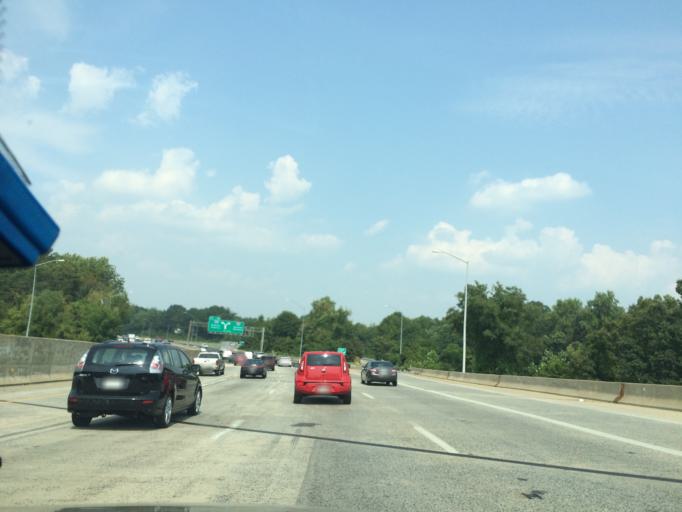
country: US
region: Maryland
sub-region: Montgomery County
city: Cabin John
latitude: 38.9843
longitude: -77.1594
